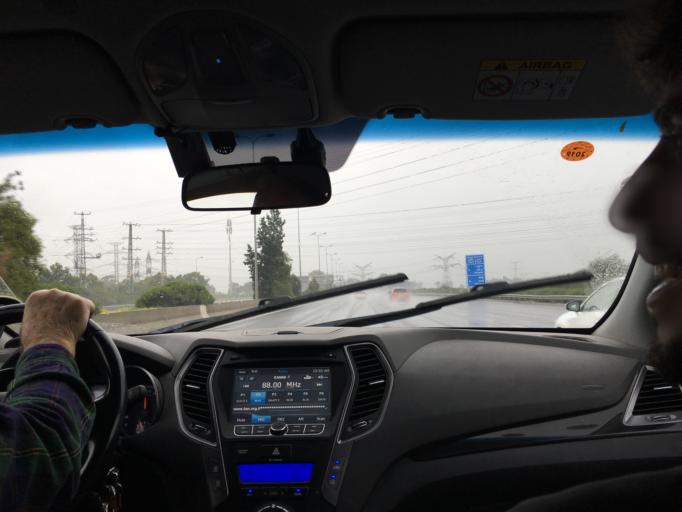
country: IL
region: Central District
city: Petah Tiqwa
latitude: 32.1193
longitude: 34.8839
